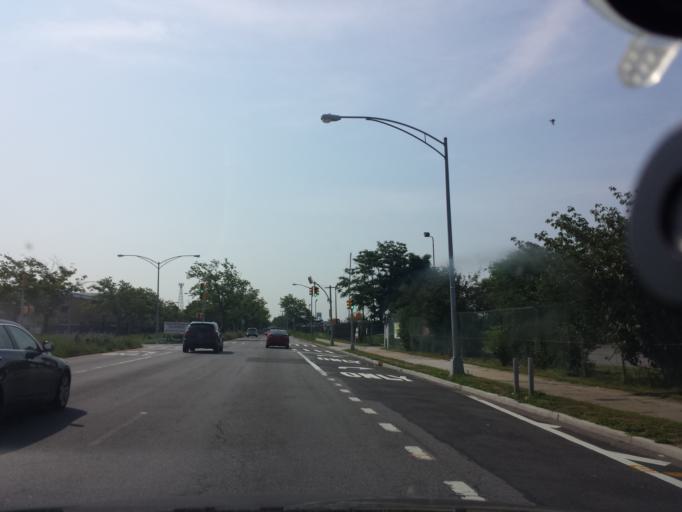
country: US
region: New York
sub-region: Kings County
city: Brooklyn
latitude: 40.5904
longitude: -73.9014
